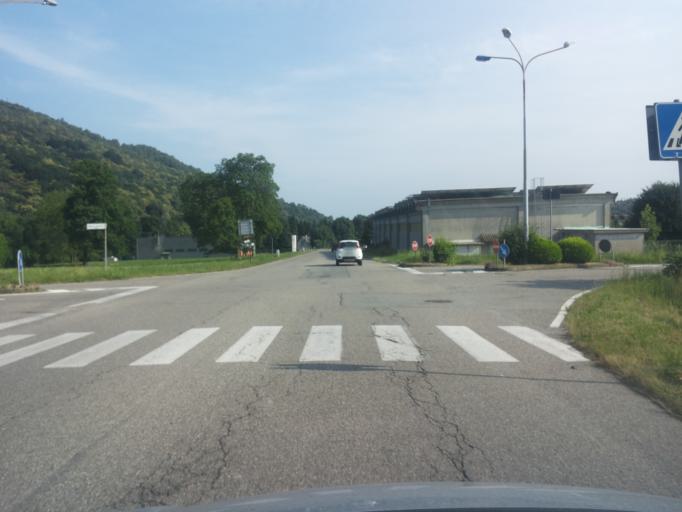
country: IT
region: Piedmont
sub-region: Provincia di Biella
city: Andorno Cacciorna
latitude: 45.6067
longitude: 8.0536
